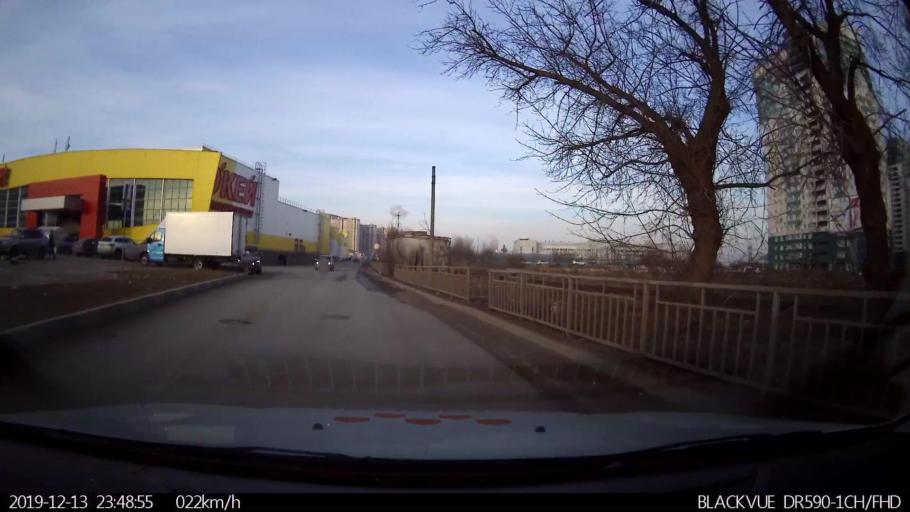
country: RU
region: Nizjnij Novgorod
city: Nizhniy Novgorod
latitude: 56.3006
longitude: 43.9494
